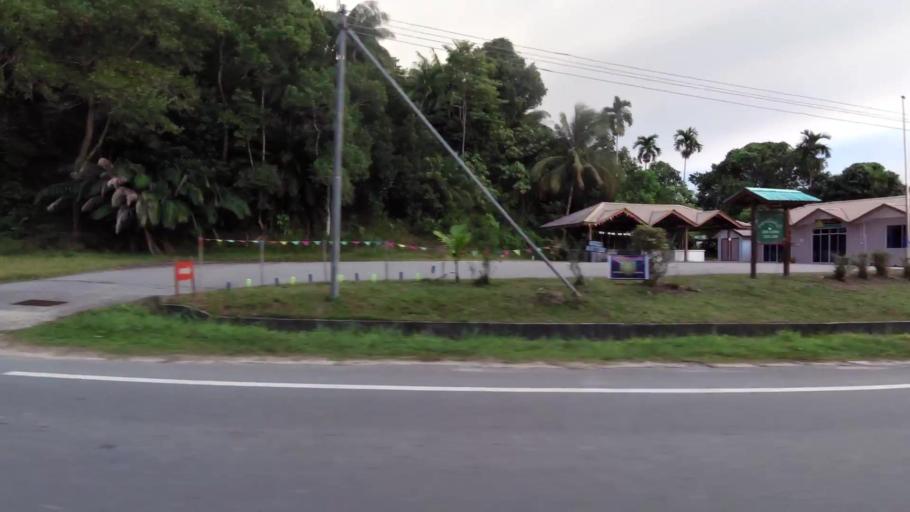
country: BN
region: Brunei and Muara
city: Bandar Seri Begawan
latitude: 4.9930
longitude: 114.9986
